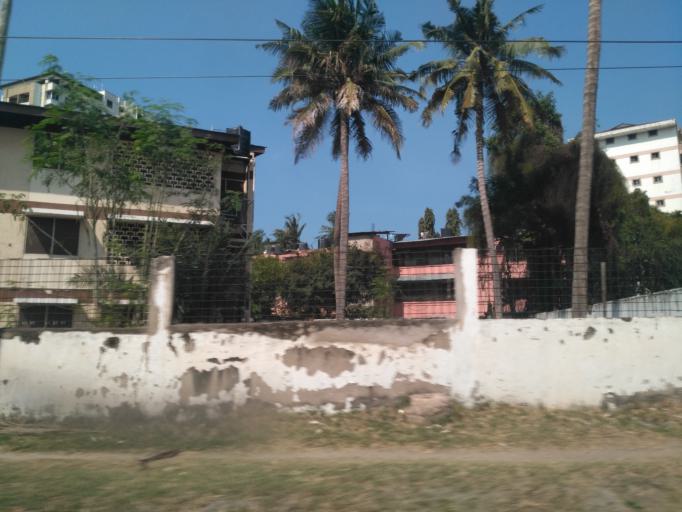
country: TZ
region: Dar es Salaam
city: Dar es Salaam
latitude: -6.8068
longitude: 39.2816
